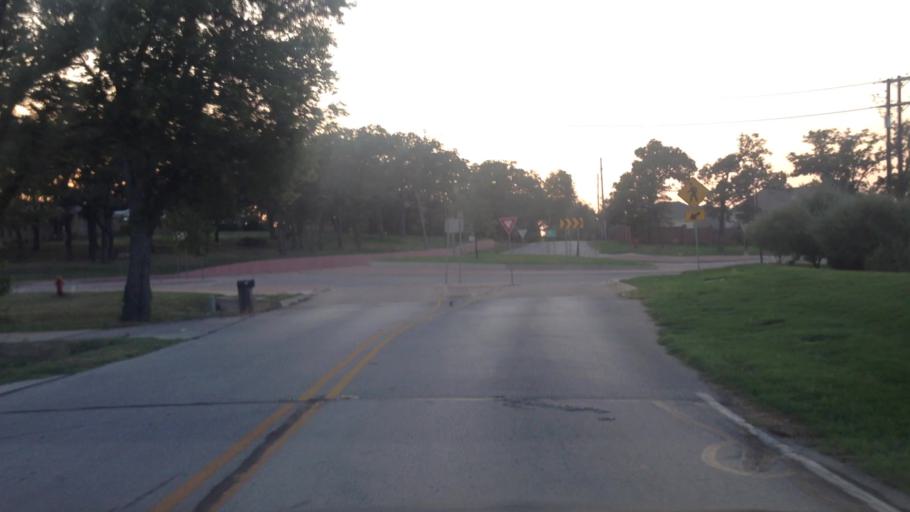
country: US
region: Texas
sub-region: Tarrant County
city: Kennedale
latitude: 32.6384
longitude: -97.2081
